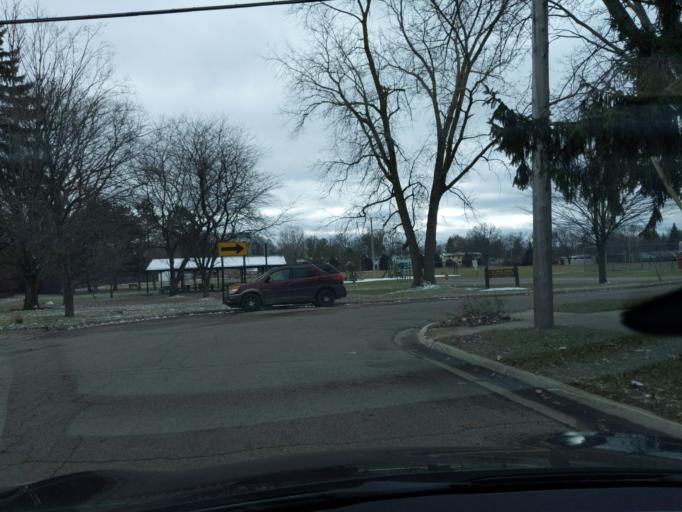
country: US
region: Michigan
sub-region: Ingham County
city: East Lansing
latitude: 42.7510
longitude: -84.5138
